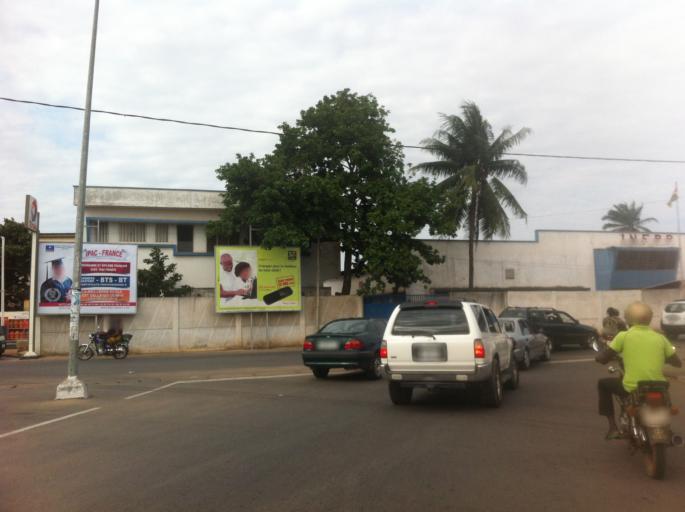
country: TG
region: Maritime
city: Lome
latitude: 6.1325
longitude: 1.2168
